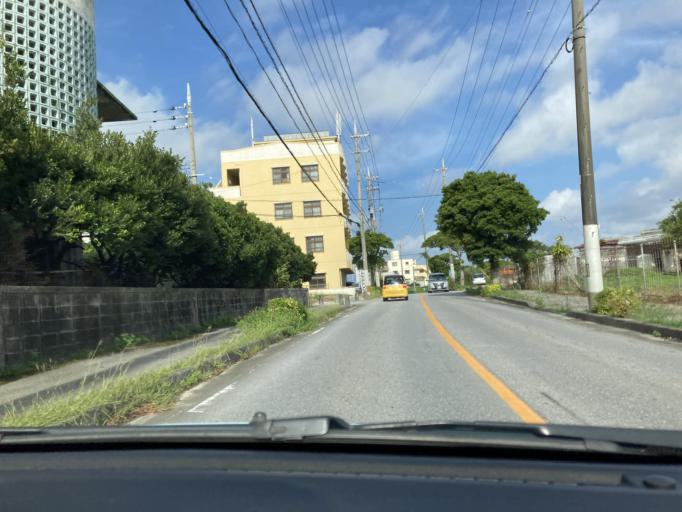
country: JP
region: Okinawa
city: Ginowan
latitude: 26.2548
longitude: 127.7726
